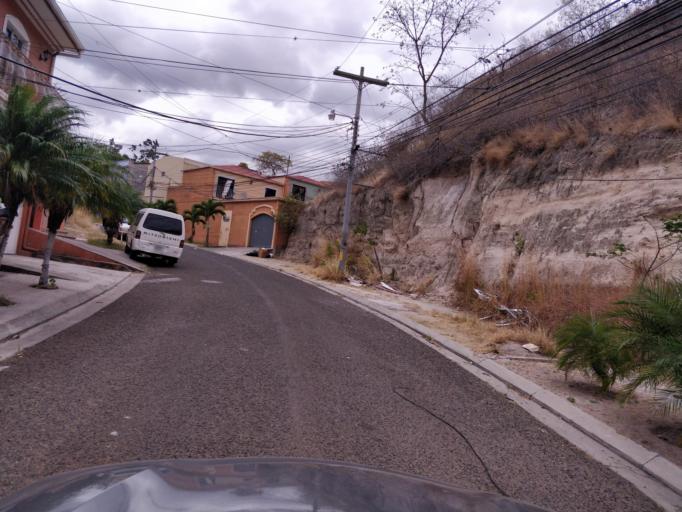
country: HN
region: Francisco Morazan
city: Yaguacire
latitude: 14.0482
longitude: -87.2180
